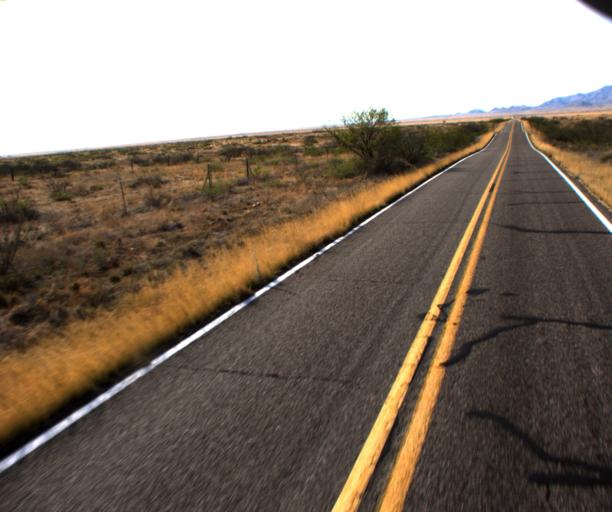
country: US
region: Arizona
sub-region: Cochise County
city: Willcox
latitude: 32.0517
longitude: -109.4926
